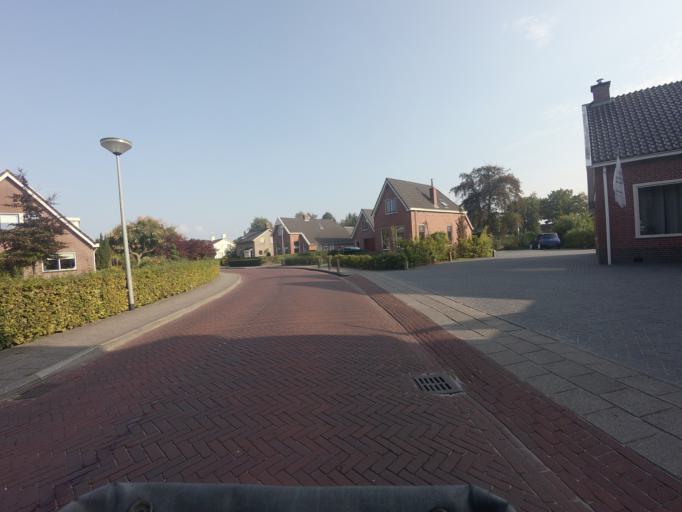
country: NL
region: Groningen
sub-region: Gemeente Haren
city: Haren
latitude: 53.1485
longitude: 6.5646
